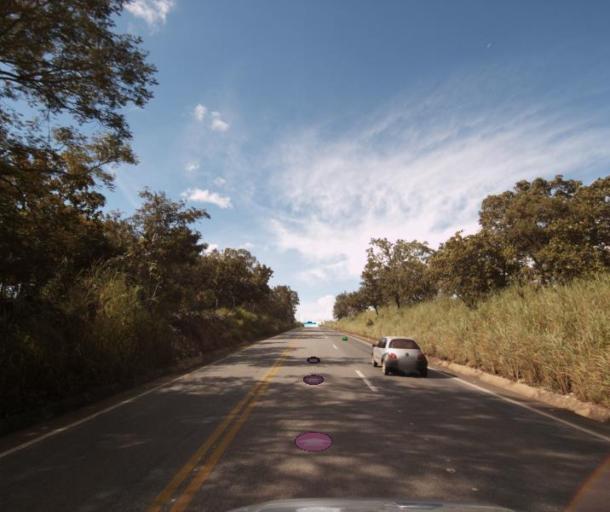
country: BR
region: Goias
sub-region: Porangatu
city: Porangatu
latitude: -13.0895
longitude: -49.1935
